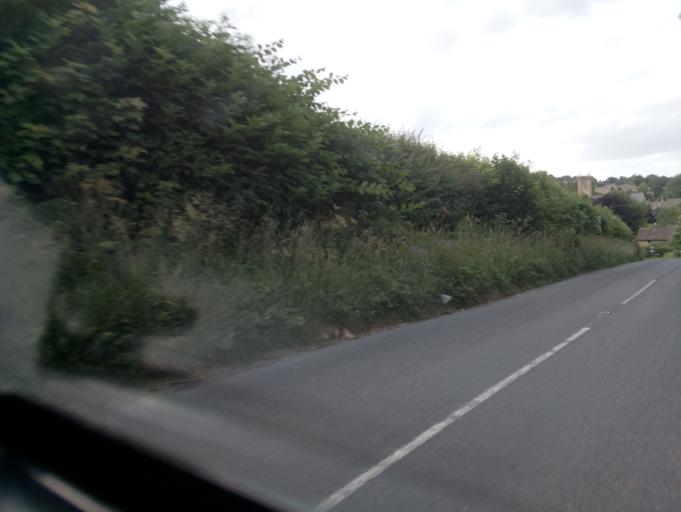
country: GB
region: England
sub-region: Gloucestershire
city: Chipping Campden
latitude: 52.0090
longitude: -1.7618
